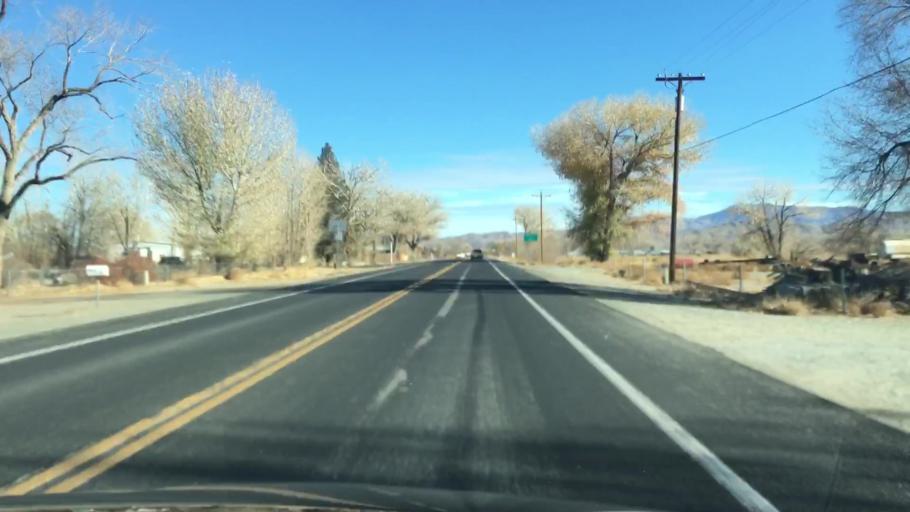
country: US
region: Nevada
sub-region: Lyon County
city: Yerington
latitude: 38.9974
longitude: -119.1577
